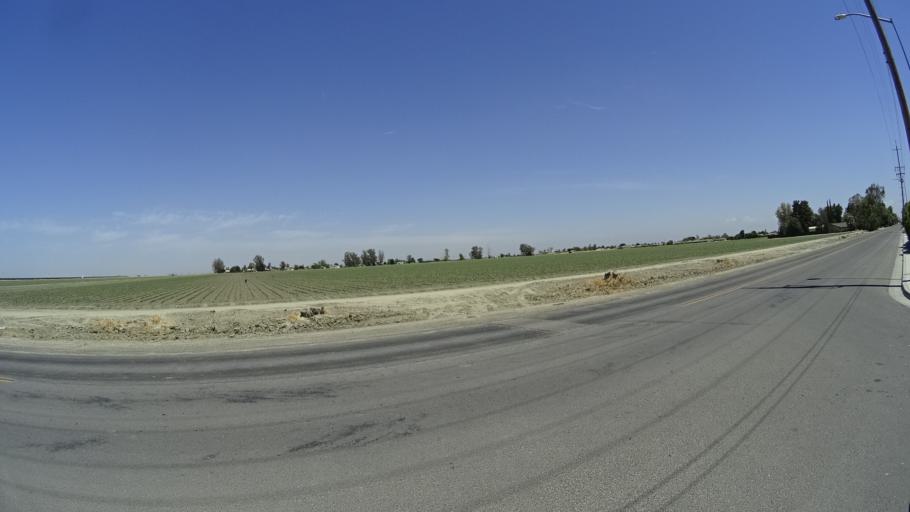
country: US
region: California
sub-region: Kings County
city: Corcoran
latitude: 36.1088
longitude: -119.5797
